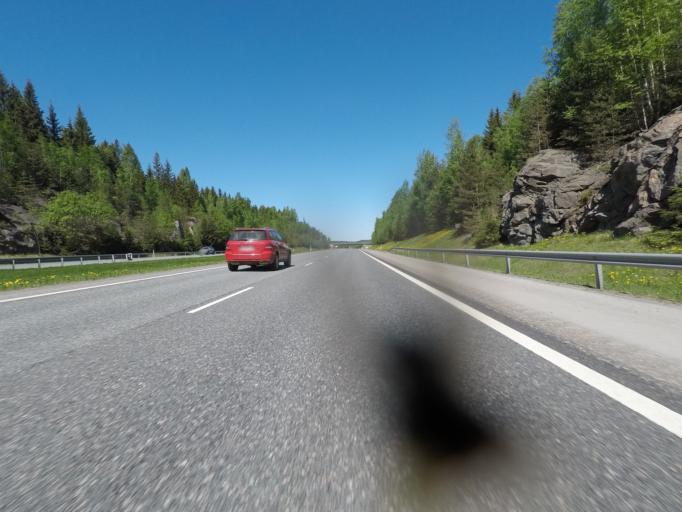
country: FI
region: Haeme
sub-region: Haemeenlinna
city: Janakkala
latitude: 60.8869
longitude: 24.5659
